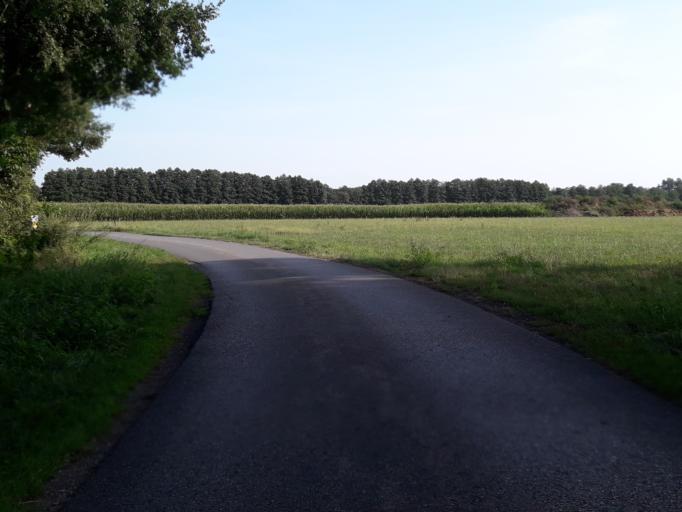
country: DE
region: North Rhine-Westphalia
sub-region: Regierungsbezirk Detmold
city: Hovelhof
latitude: 51.7817
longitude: 8.6352
